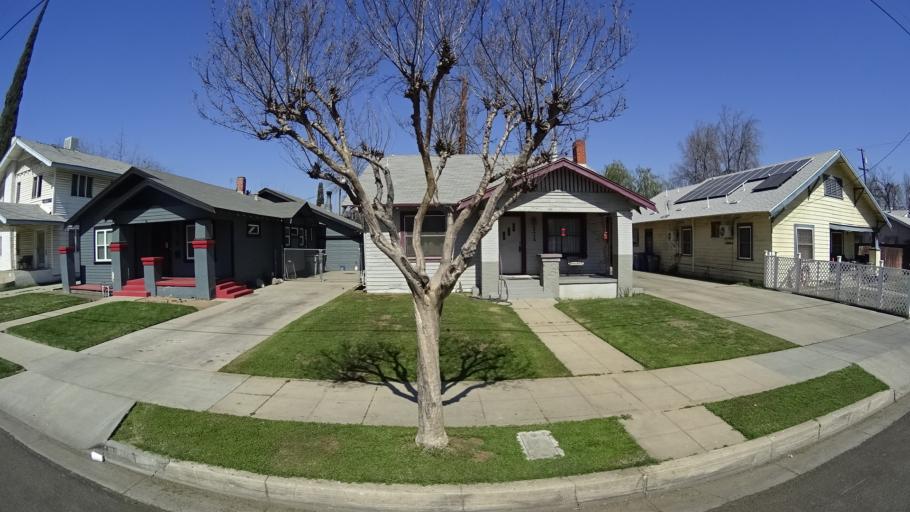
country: US
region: California
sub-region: Fresno County
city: Fresno
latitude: 36.7549
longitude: -119.8015
